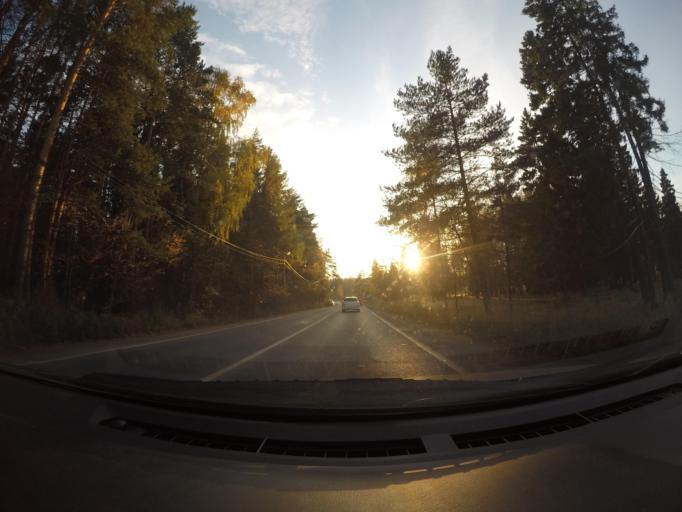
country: RU
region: Moskovskaya
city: Firsanovka
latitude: 55.9639
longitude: 37.2549
